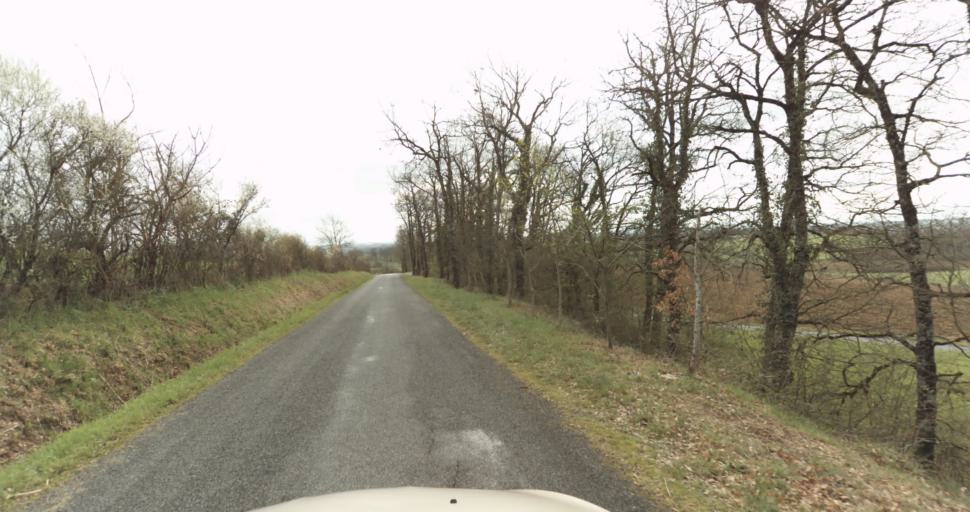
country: FR
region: Midi-Pyrenees
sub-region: Departement du Tarn
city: Frejairolles
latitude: 43.8656
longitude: 2.2137
